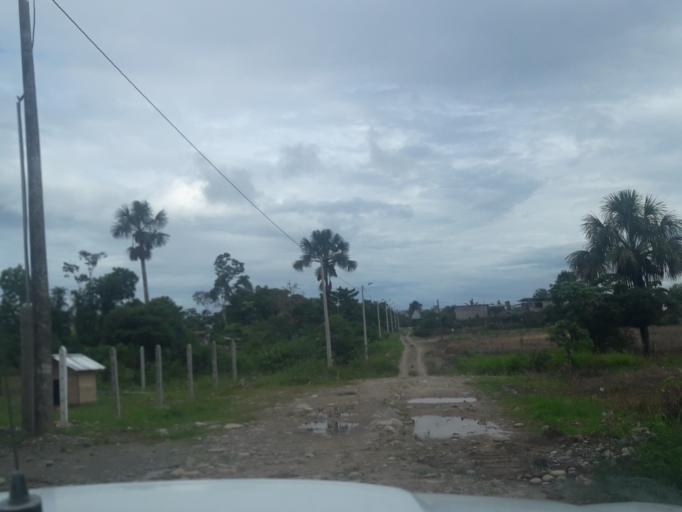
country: EC
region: Napo
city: Tena
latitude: -0.9527
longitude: -77.8158
